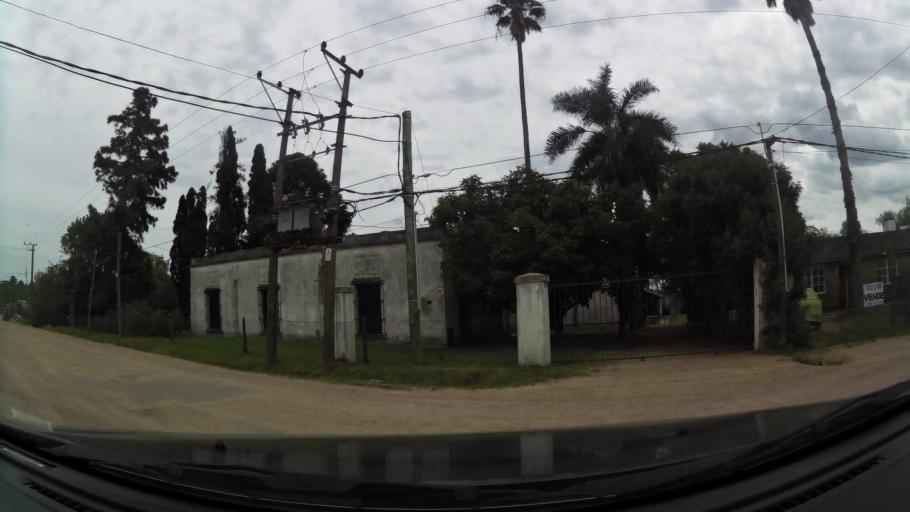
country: UY
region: Canelones
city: Las Piedras
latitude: -34.7168
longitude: -56.2020
